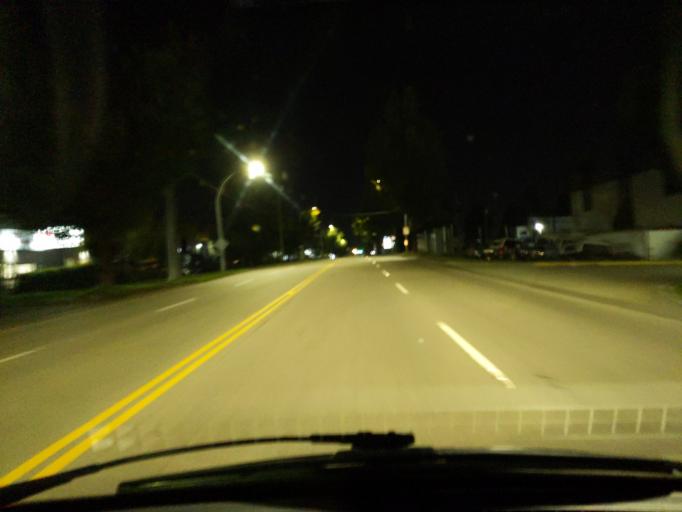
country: CA
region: British Columbia
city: Walnut Grove
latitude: 49.1771
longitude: -122.6805
